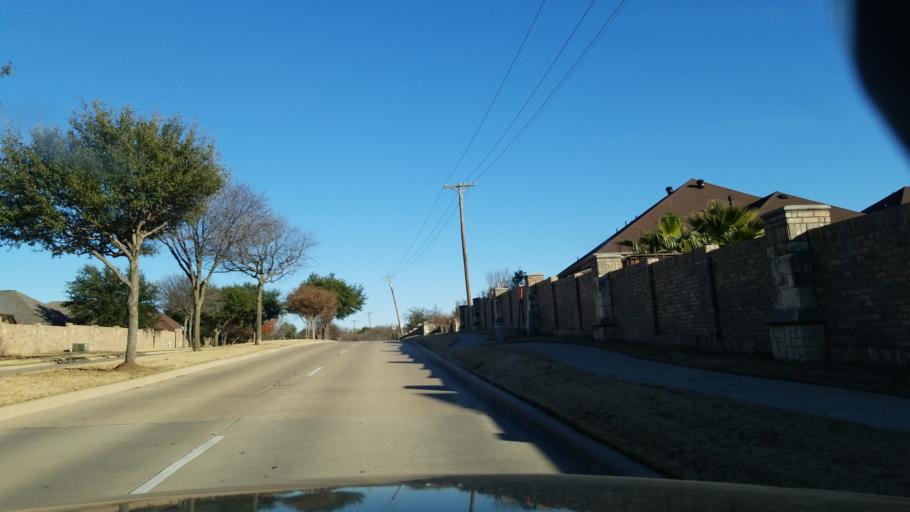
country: US
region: Texas
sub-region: Denton County
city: Corinth
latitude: 33.1550
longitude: -97.0828
